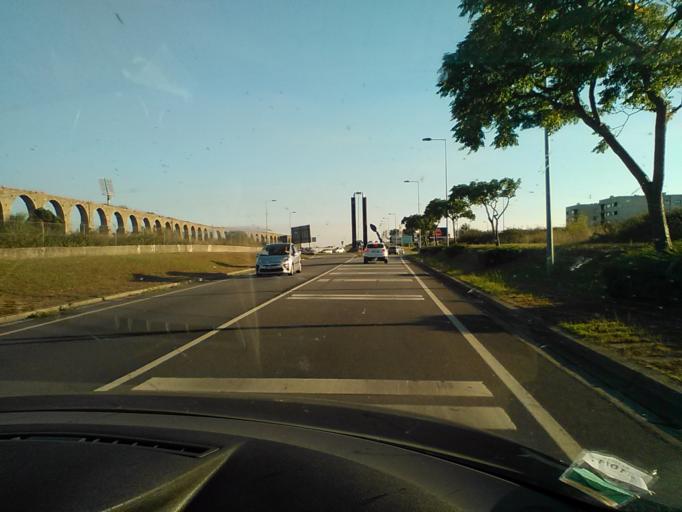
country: PT
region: Porto
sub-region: Vila do Conde
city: Vila do Conde
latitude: 41.3661
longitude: -8.7412
